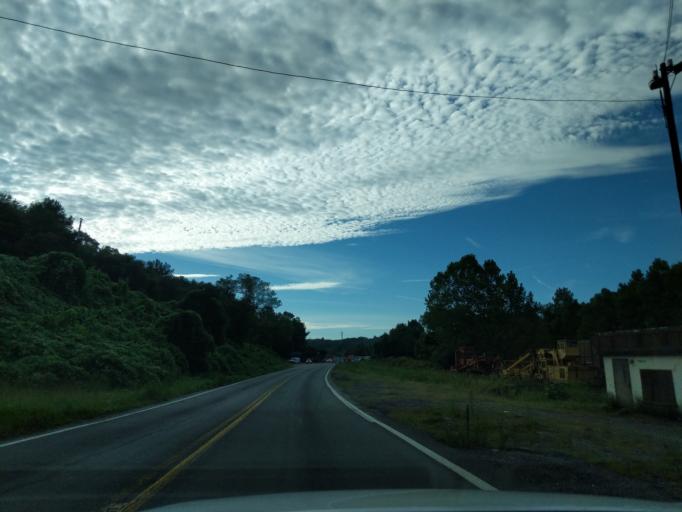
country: US
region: Georgia
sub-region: Fannin County
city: McCaysville
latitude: 34.9920
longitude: -84.3764
